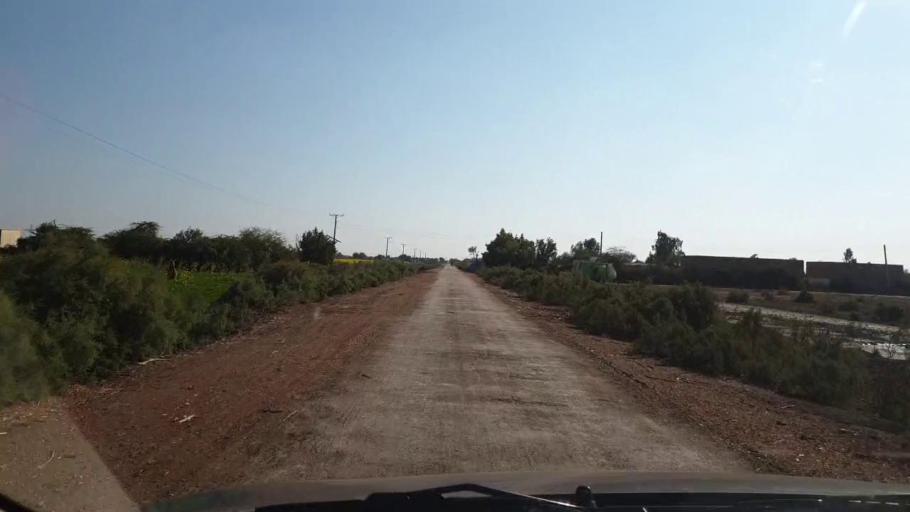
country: PK
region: Sindh
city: Sinjhoro
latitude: 25.9939
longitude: 68.8394
